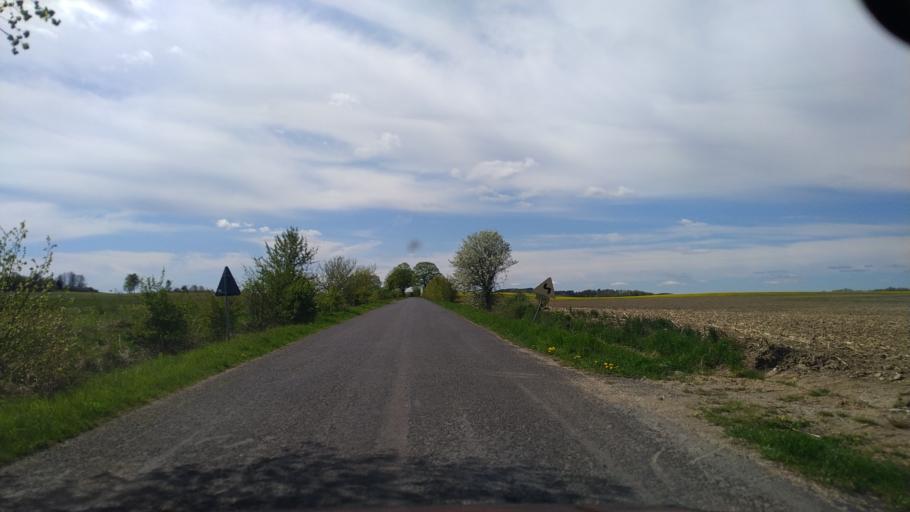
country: PL
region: West Pomeranian Voivodeship
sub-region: Powiat walecki
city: Walcz
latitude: 53.3536
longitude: 16.3264
